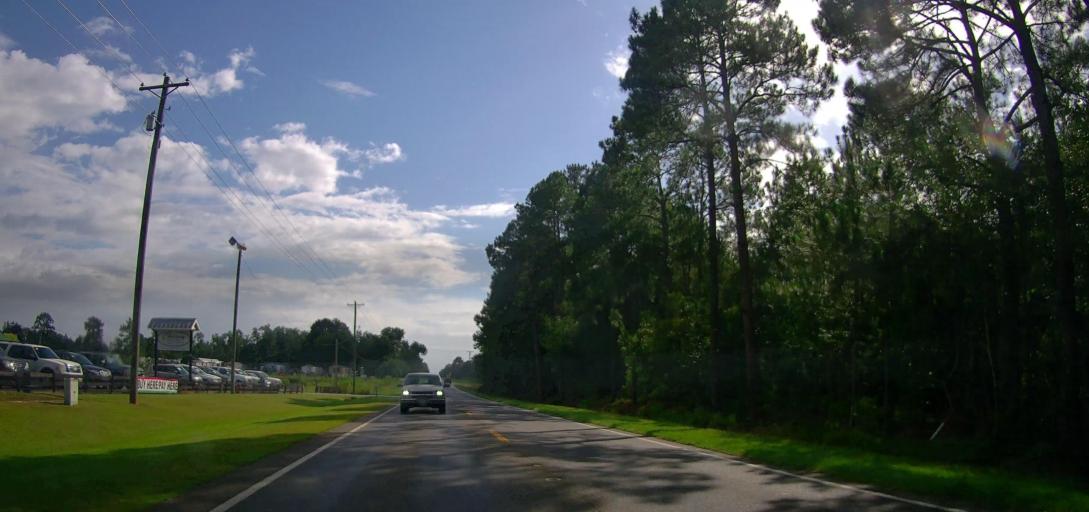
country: US
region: Georgia
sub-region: Coffee County
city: Douglas
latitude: 31.4839
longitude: -82.8638
